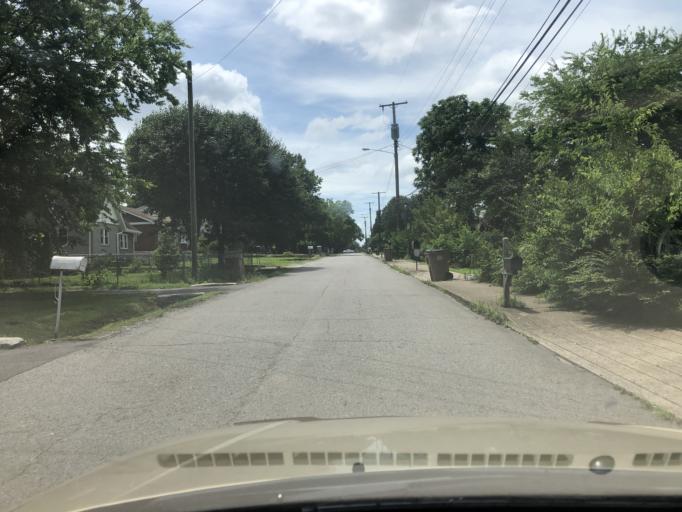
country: US
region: Tennessee
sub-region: Davidson County
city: Goodlettsville
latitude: 36.2571
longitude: -86.7111
